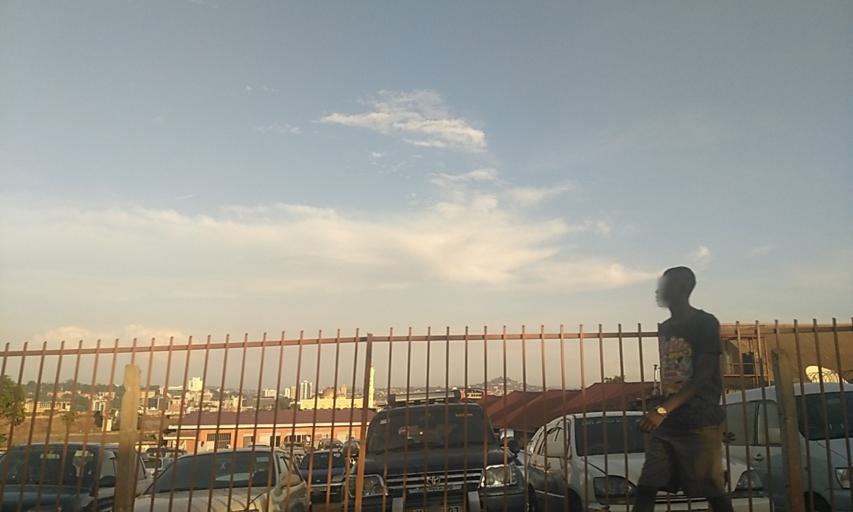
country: UG
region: Central Region
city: Kampala Central Division
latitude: 0.3170
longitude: 32.5618
